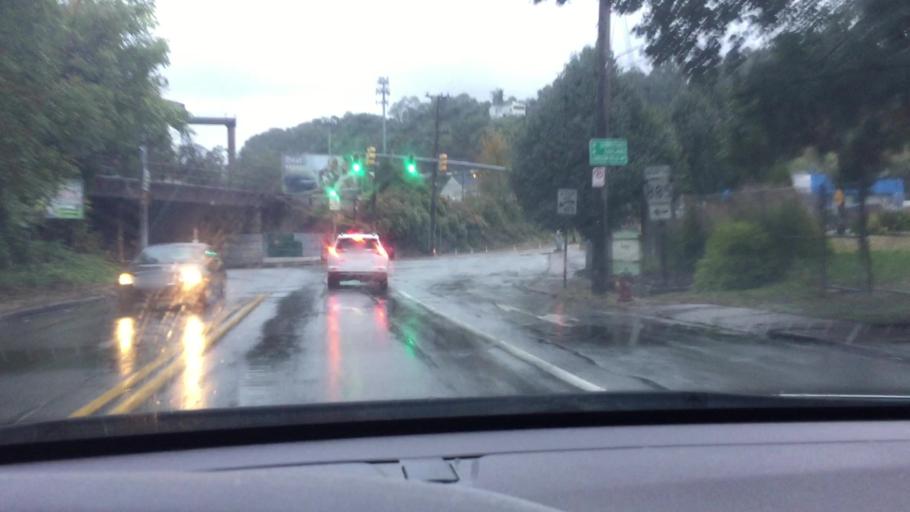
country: US
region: Pennsylvania
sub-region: Allegheny County
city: Bloomfield
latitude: 40.4245
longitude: -79.9518
